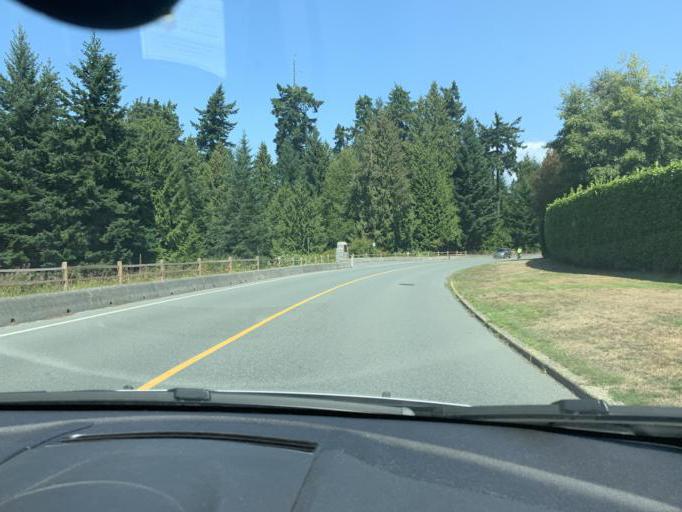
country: CA
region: British Columbia
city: West End
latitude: 49.2729
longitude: -123.2542
